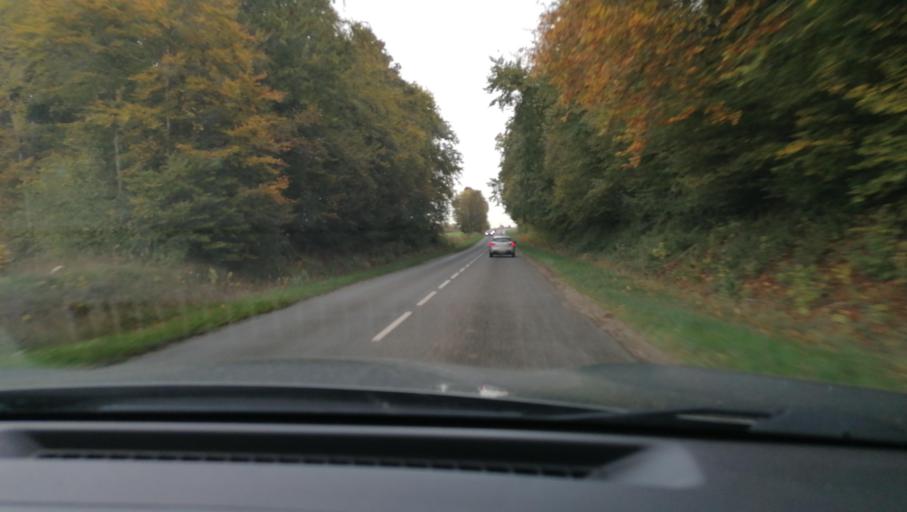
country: FR
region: Picardie
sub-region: Departement de la Somme
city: Picquigny
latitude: 49.8906
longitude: 2.1255
